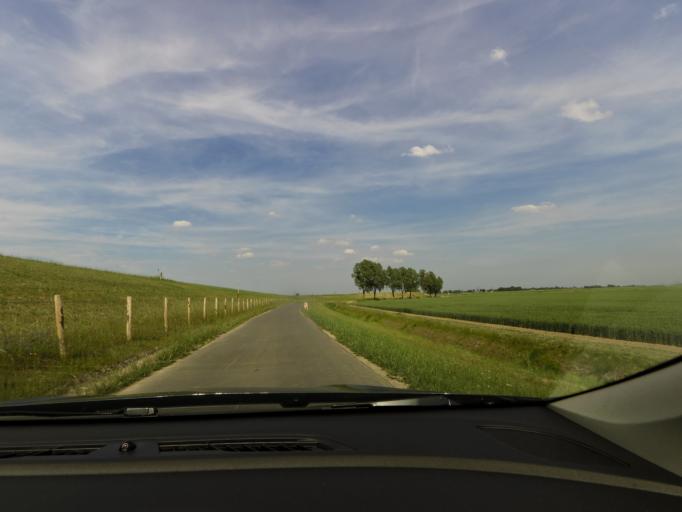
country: NL
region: South Holland
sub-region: Gemeente Spijkenisse
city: Spijkenisse
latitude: 51.8066
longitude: 4.3046
